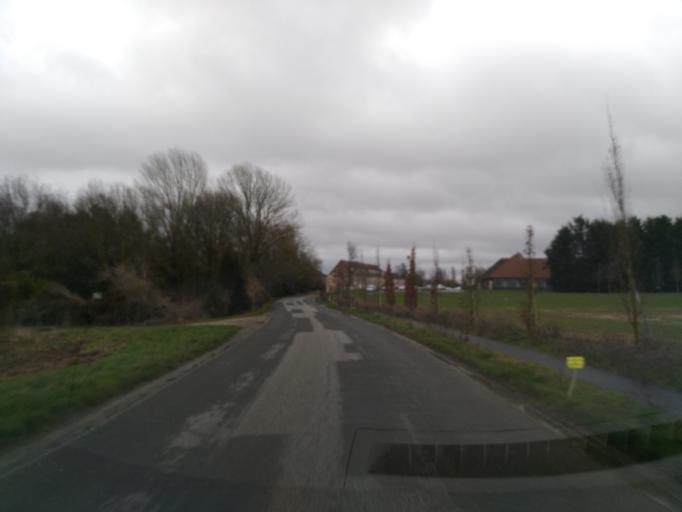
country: FR
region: Ile-de-France
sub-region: Departement des Yvelines
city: Thoiry
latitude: 48.8706
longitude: 1.7933
